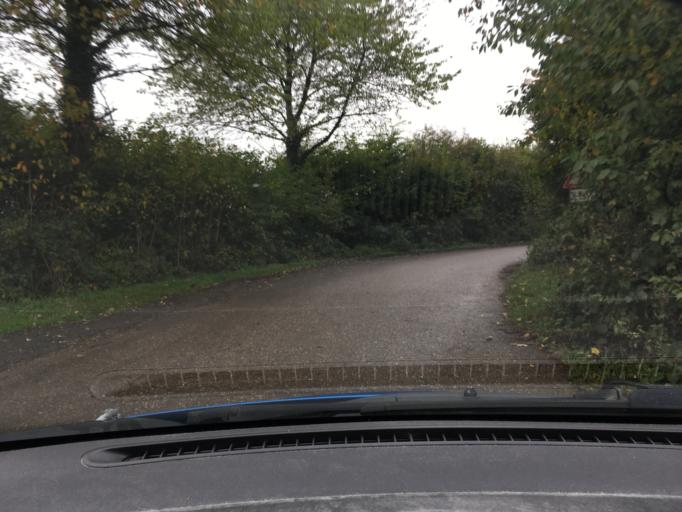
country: DE
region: Schleswig-Holstein
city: Bosdorf
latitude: 54.1044
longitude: 10.4786
